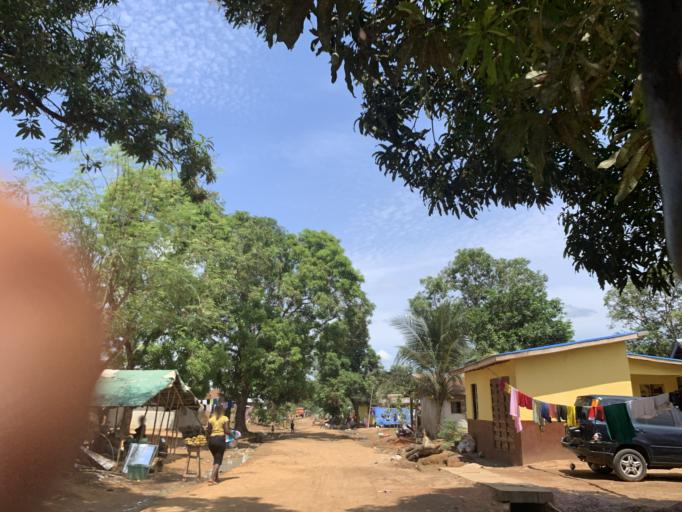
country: SL
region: Western Area
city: Waterloo
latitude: 8.3392
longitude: -13.0474
